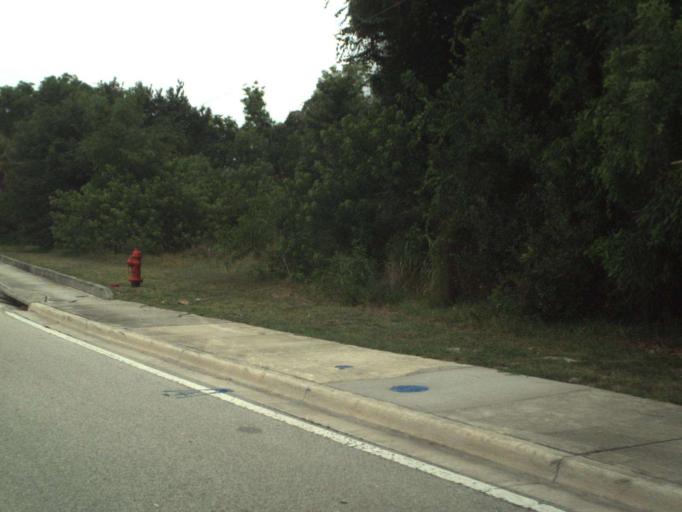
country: US
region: Florida
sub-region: Saint Lucie County
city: River Park
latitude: 27.3332
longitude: -80.3513
